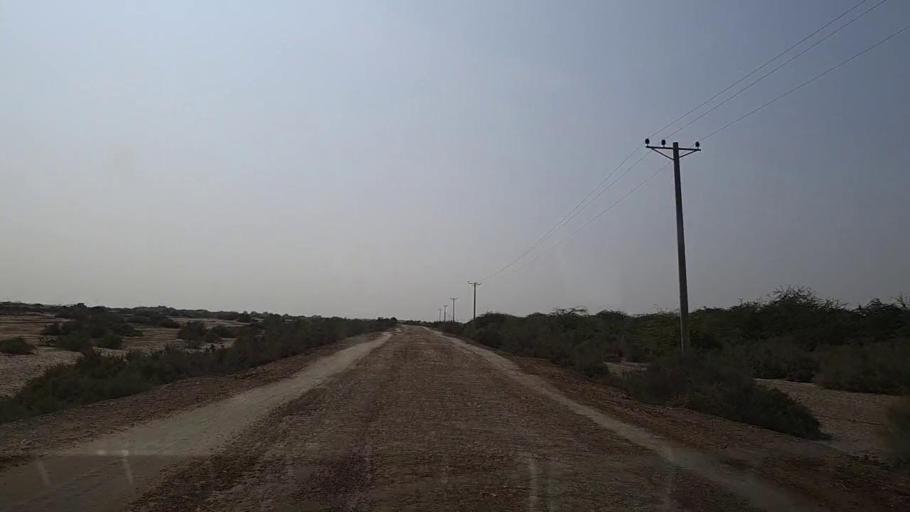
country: PK
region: Sindh
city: Mirpur Sakro
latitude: 24.5361
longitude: 67.5964
